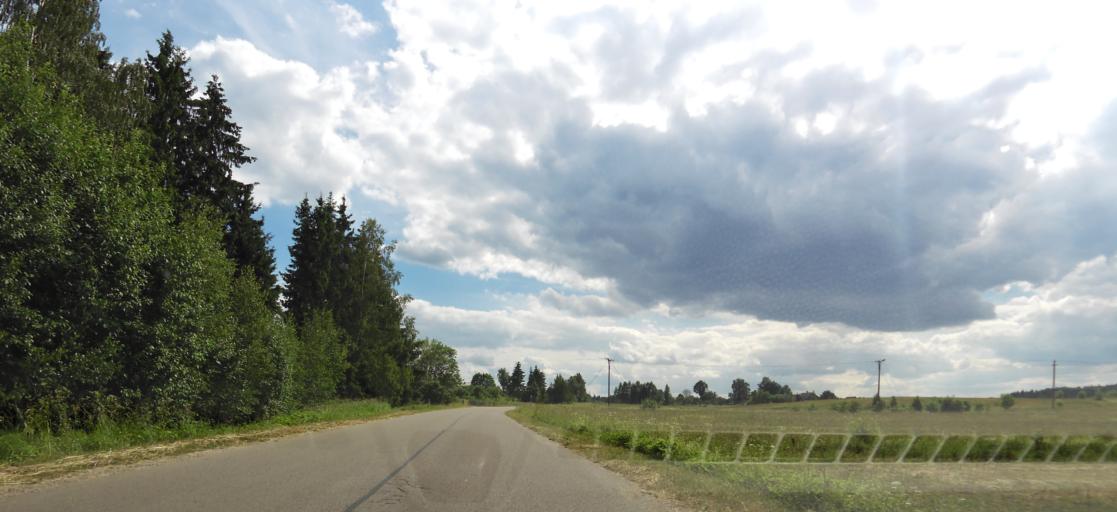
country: LT
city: Skaidiskes
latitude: 54.5366
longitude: 25.6450
